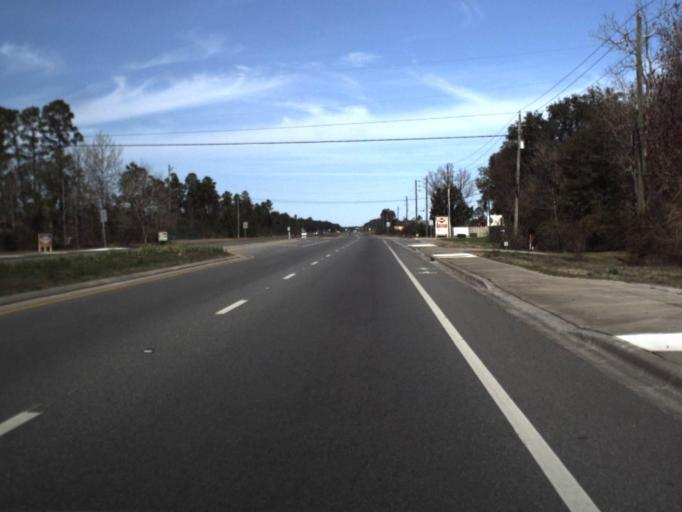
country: US
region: Florida
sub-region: Bay County
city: Lynn Haven
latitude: 30.2941
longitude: -85.6434
